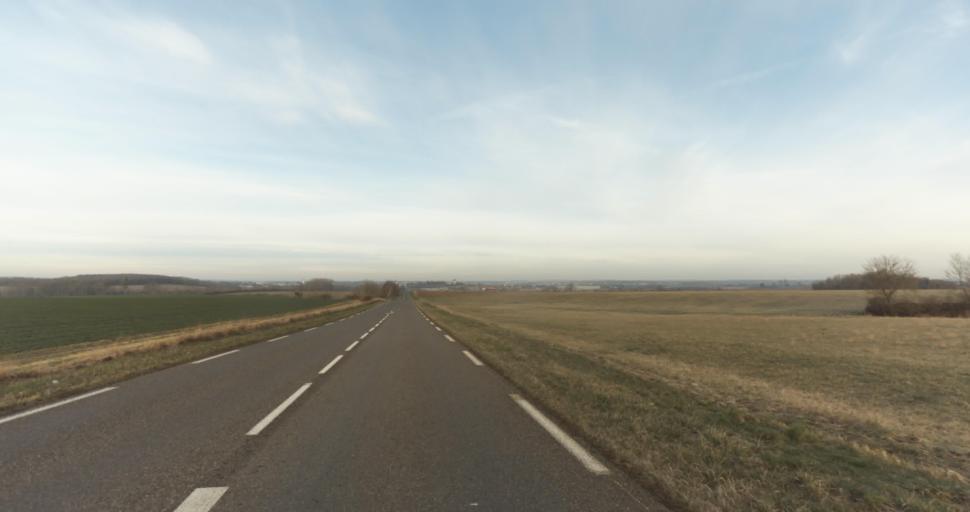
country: FR
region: Lorraine
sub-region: Departement de Meurthe-et-Moselle
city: Doncourt-les-Conflans
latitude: 49.1471
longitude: 5.9208
